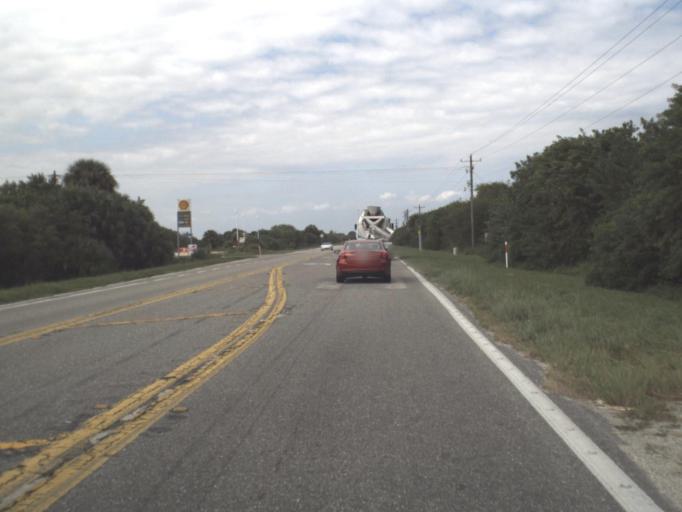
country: US
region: Florida
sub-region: Glades County
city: Moore Haven
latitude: 26.7684
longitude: -81.2106
